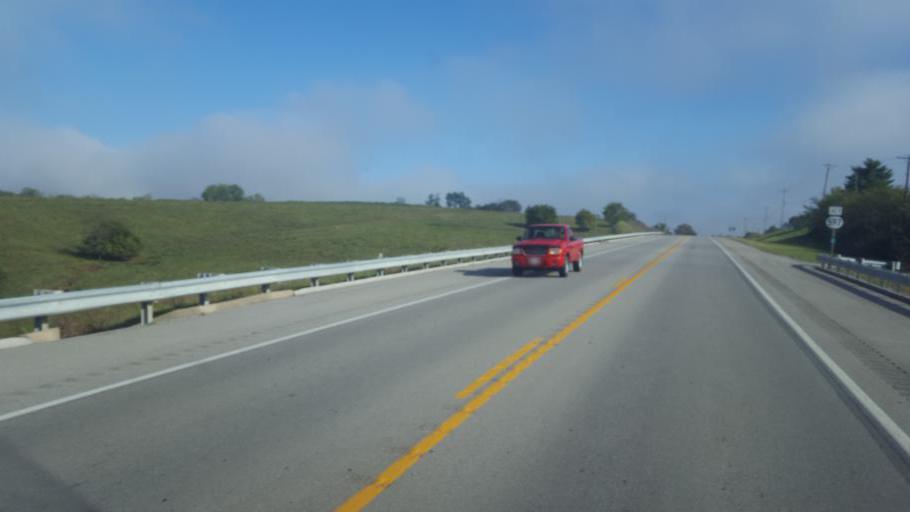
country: US
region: Kentucky
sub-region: Fleming County
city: Flemingsburg
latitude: 38.5200
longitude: -83.7563
